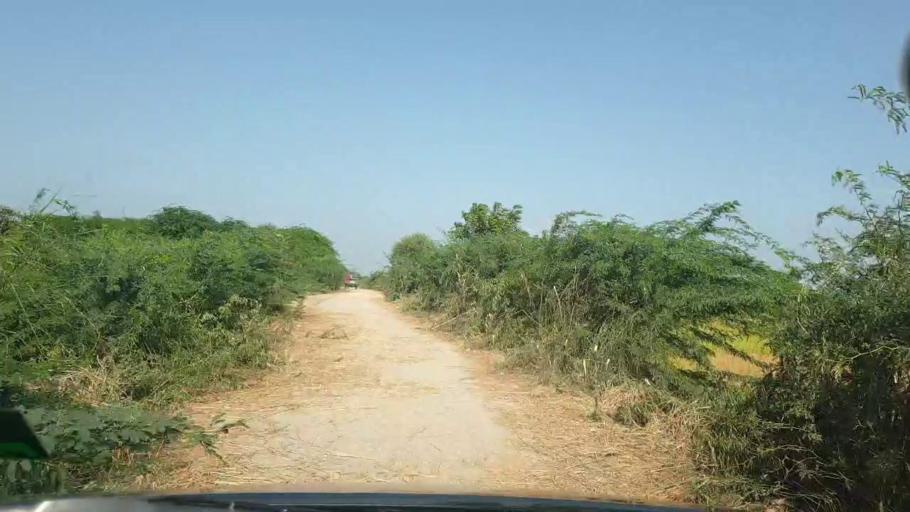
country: PK
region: Sindh
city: Tando Bago
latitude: 24.7721
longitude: 68.9544
